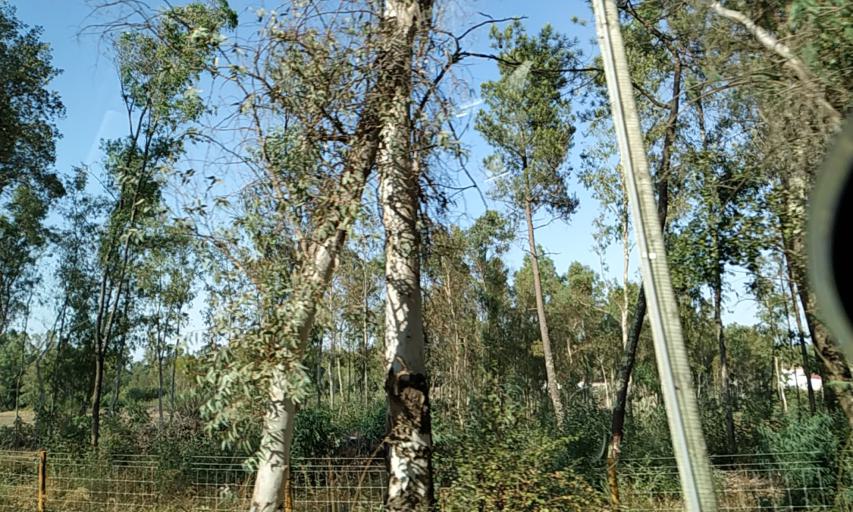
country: PT
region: Santarem
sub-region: Coruche
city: Coruche
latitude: 39.0005
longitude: -8.5578
